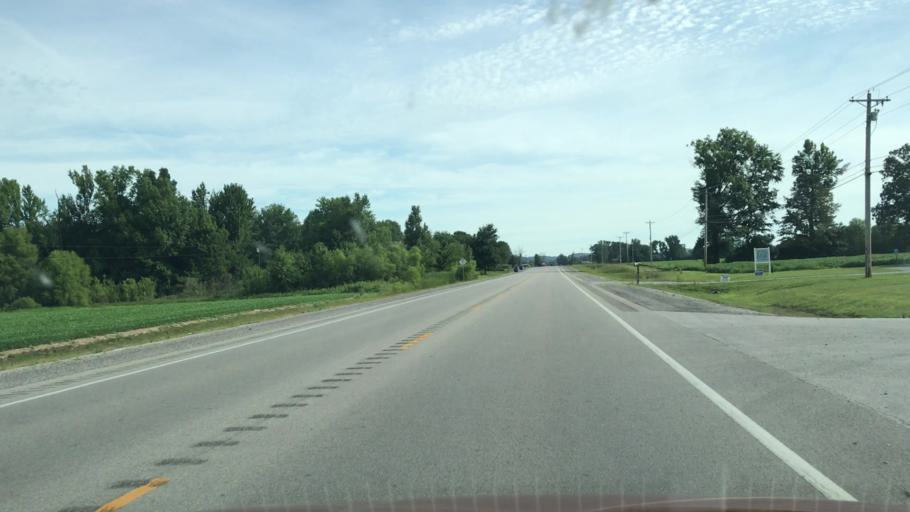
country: US
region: Kentucky
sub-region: Edmonson County
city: Brownsville
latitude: 37.1332
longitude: -86.2333
